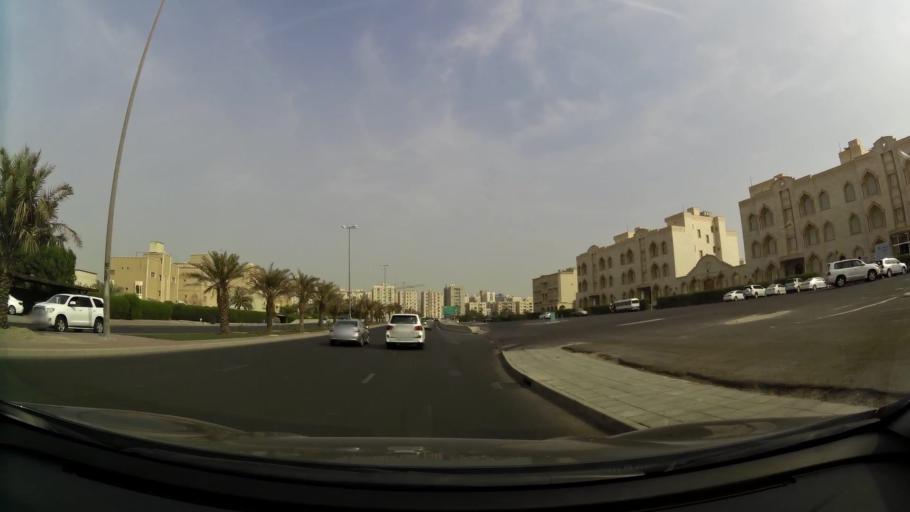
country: KW
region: Al Farwaniyah
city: Al Farwaniyah
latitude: 29.2798
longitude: 47.9455
